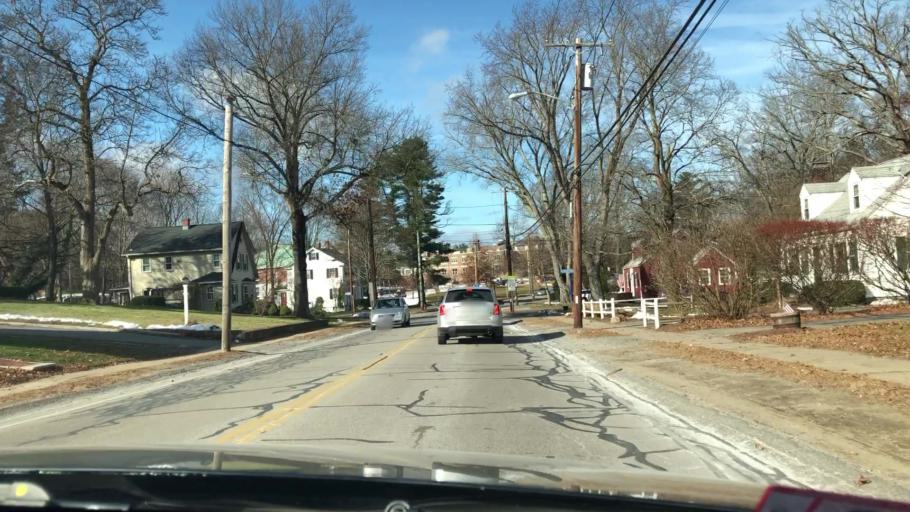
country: US
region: Massachusetts
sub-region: Norfolk County
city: Walpole
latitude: 42.1342
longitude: -71.2449
